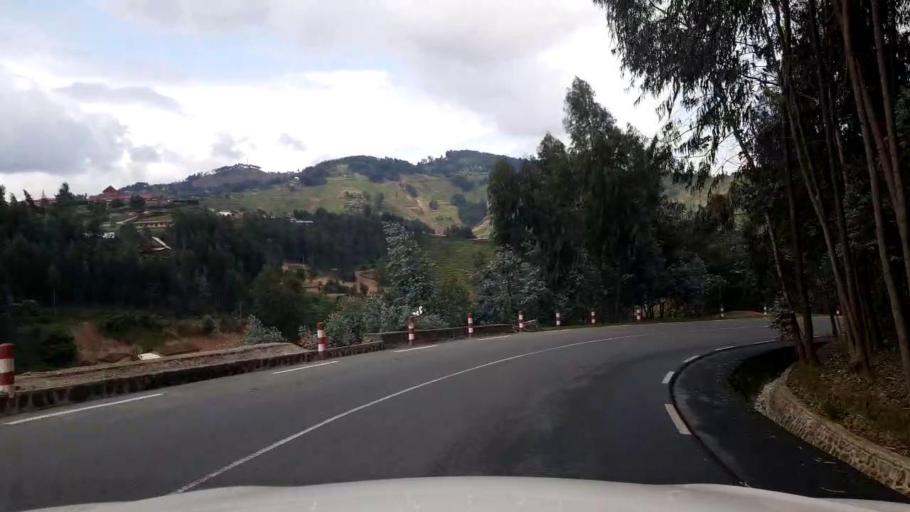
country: RW
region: Northern Province
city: Musanze
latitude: -1.6863
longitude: 29.5224
